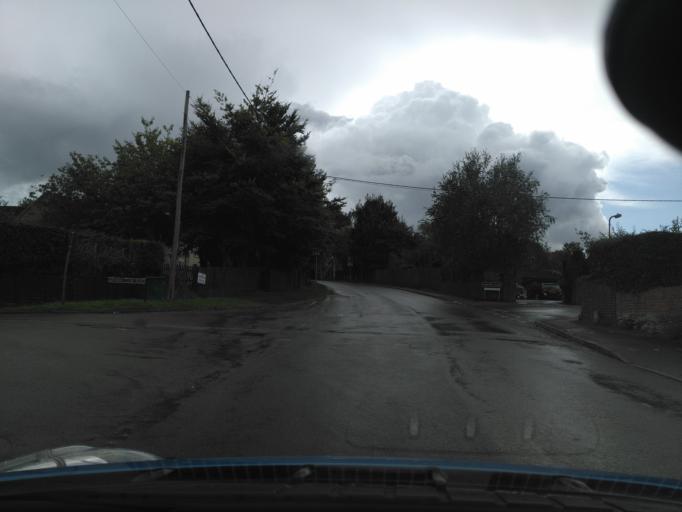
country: GB
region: England
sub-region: Oxfordshire
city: Wheatley
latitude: 51.7462
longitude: -1.1395
